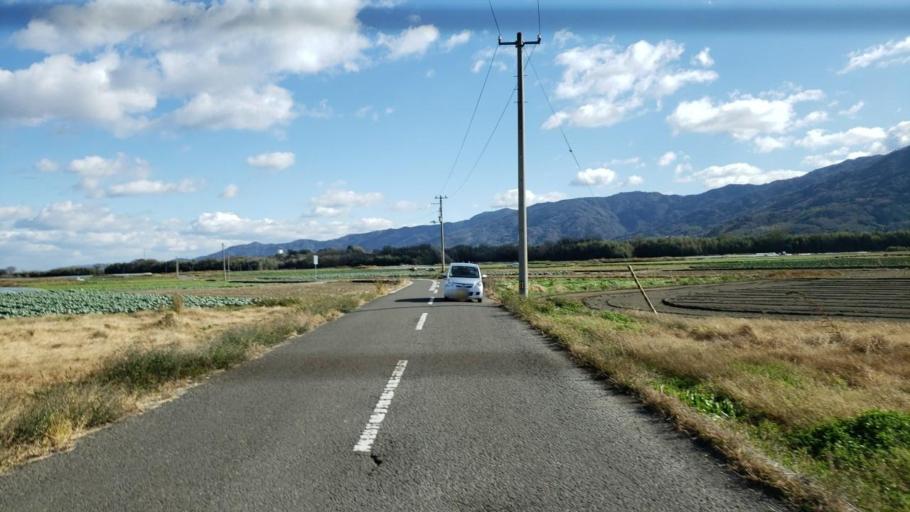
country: JP
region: Tokushima
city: Kamojimacho-jogejima
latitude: 34.0705
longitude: 134.3048
